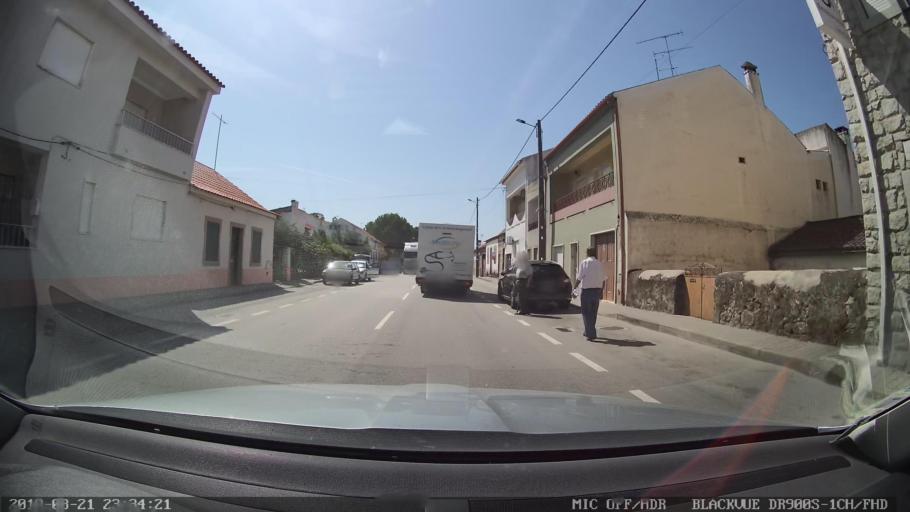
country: PT
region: Guarda
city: Alcains
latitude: 39.8820
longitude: -7.3967
